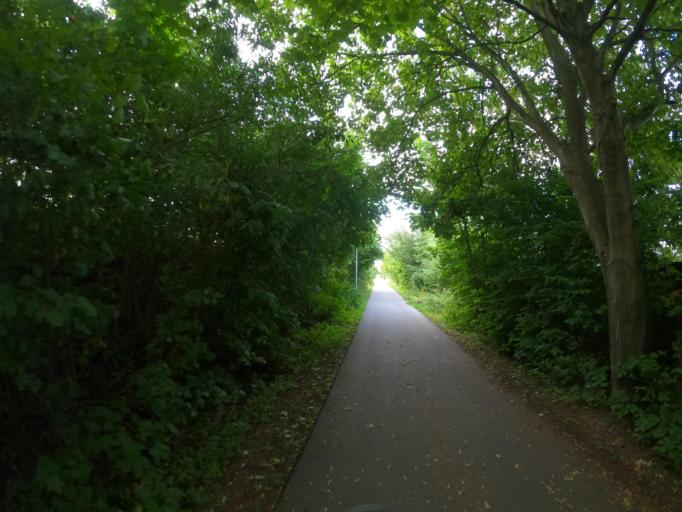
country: SE
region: Skane
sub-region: Lunds Kommun
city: Lund
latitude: 55.6838
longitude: 13.1903
